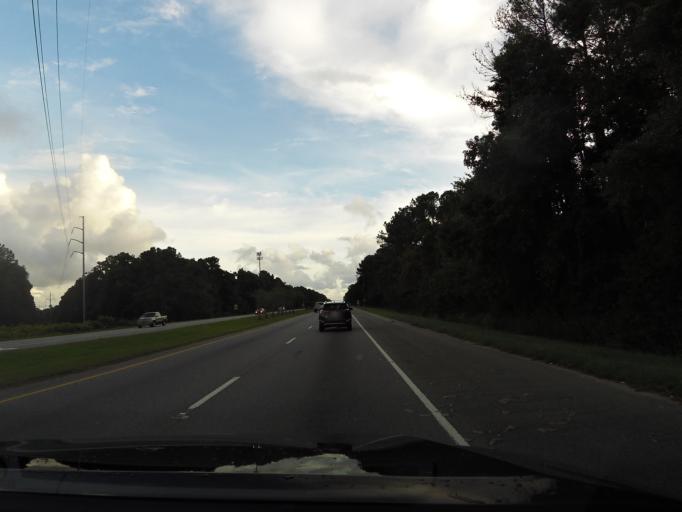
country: US
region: Georgia
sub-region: Glynn County
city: Dock Junction
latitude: 31.2303
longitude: -81.4982
